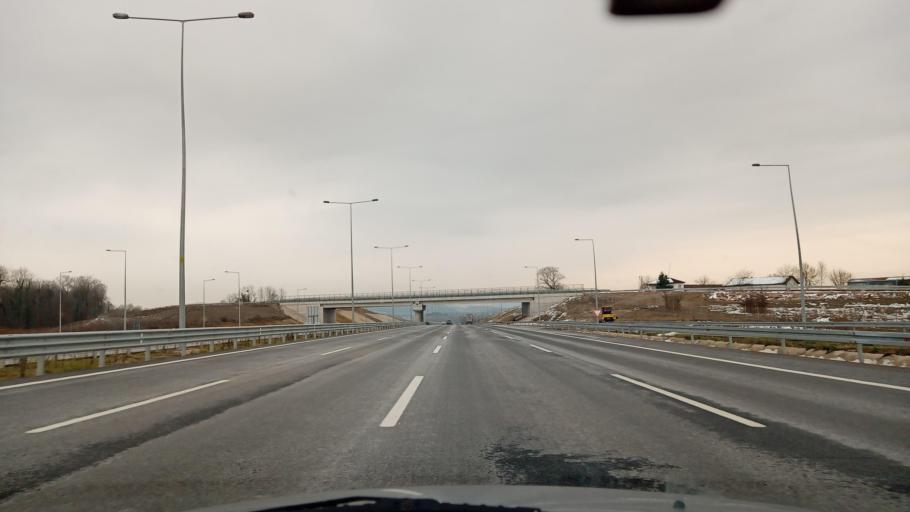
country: TR
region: Sakarya
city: Kazimpasa
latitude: 40.8439
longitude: 30.2883
